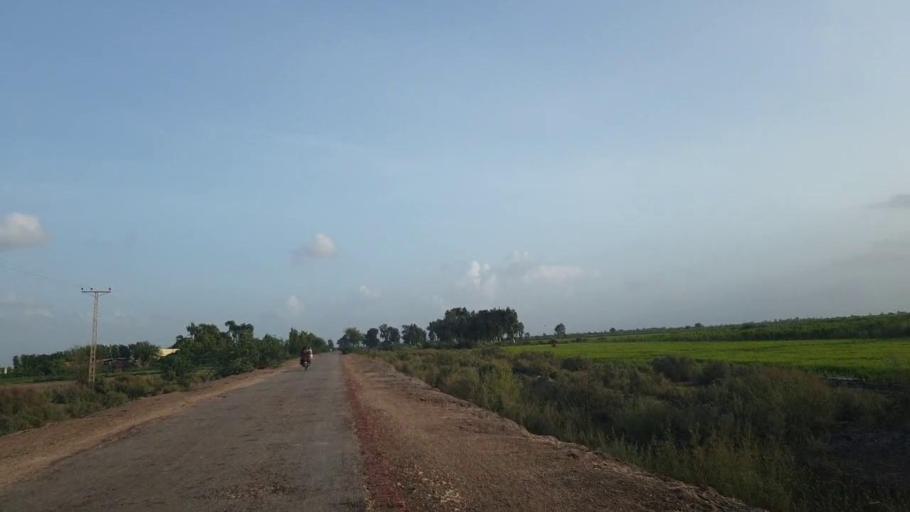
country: PK
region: Sindh
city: Kadhan
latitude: 24.6179
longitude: 69.1158
